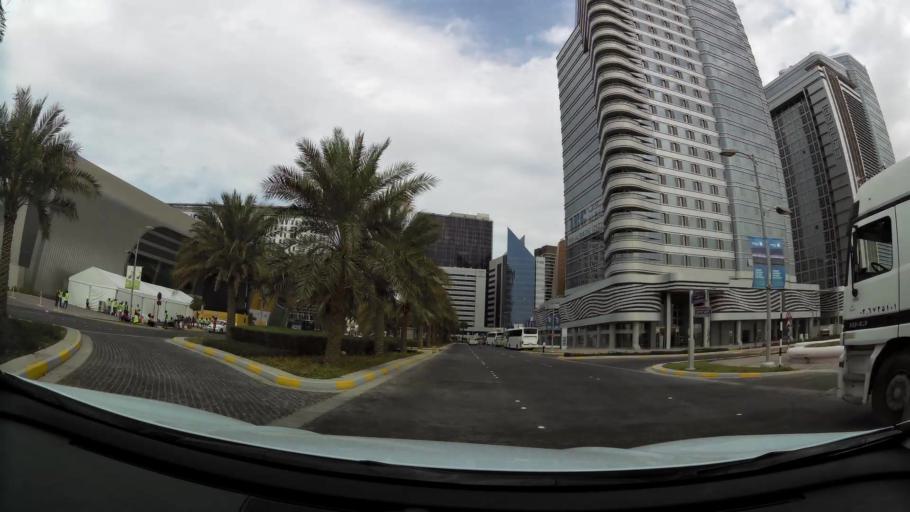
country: AE
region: Abu Dhabi
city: Abu Dhabi
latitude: 24.4177
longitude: 54.4393
